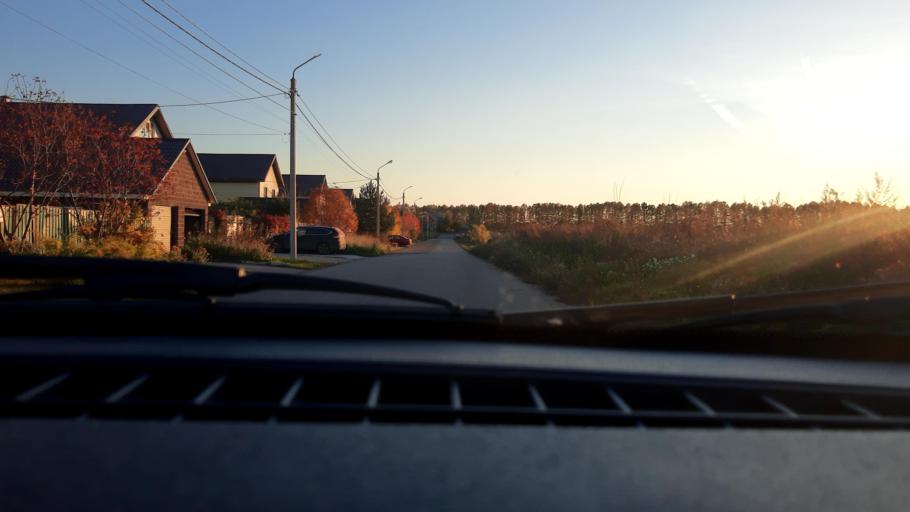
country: RU
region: Bashkortostan
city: Ufa
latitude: 54.8579
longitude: 56.0144
